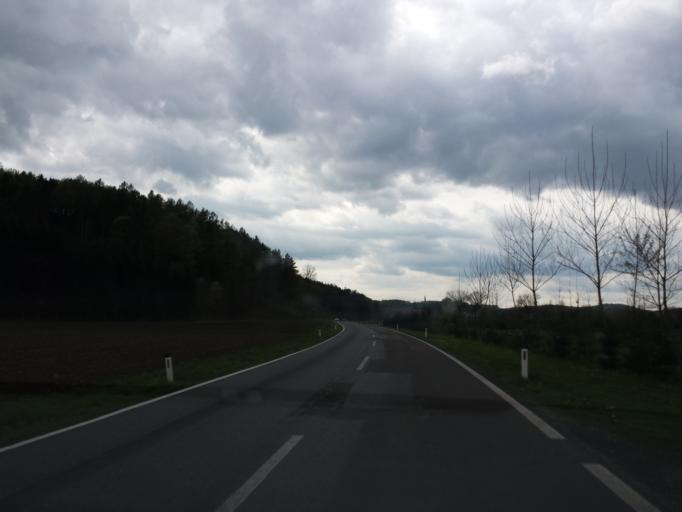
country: AT
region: Styria
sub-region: Politischer Bezirk Suedoststeiermark
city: Hatzendorf
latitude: 46.9942
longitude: 15.9671
